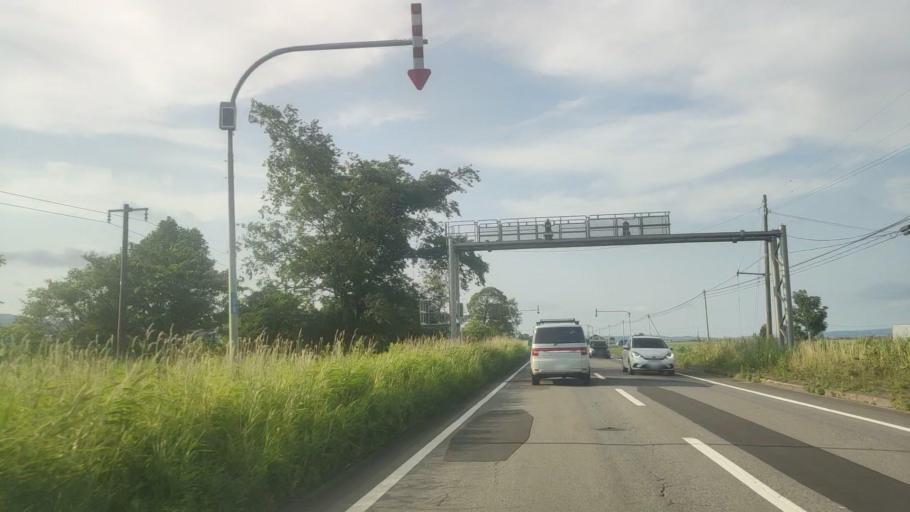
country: JP
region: Hokkaido
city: Chitose
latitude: 42.9593
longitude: 141.7980
